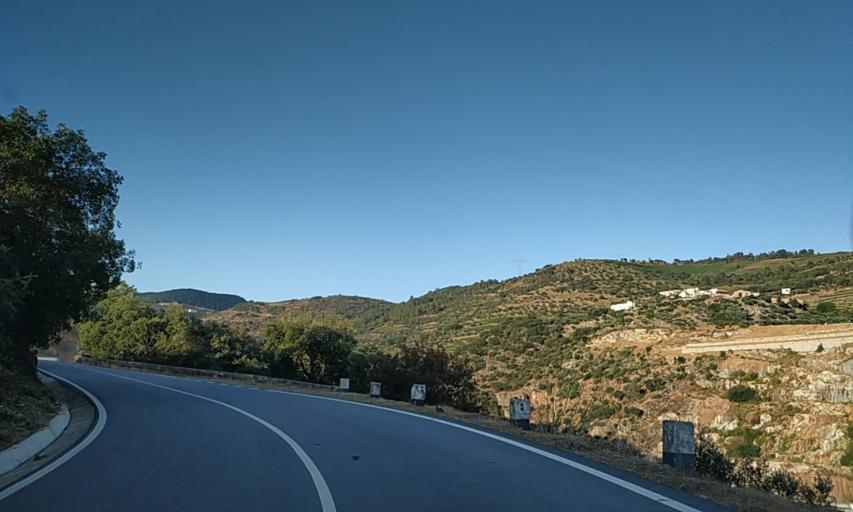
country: PT
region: Viseu
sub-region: Sao Joao da Pesqueira
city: Sao Joao da Pesqueira
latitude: 41.2176
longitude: -7.4261
